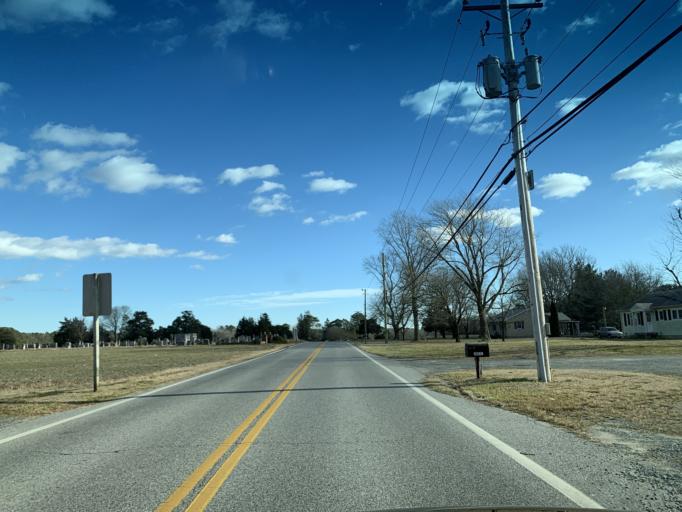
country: US
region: Maryland
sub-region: Worcester County
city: Berlin
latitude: 38.3197
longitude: -75.2004
